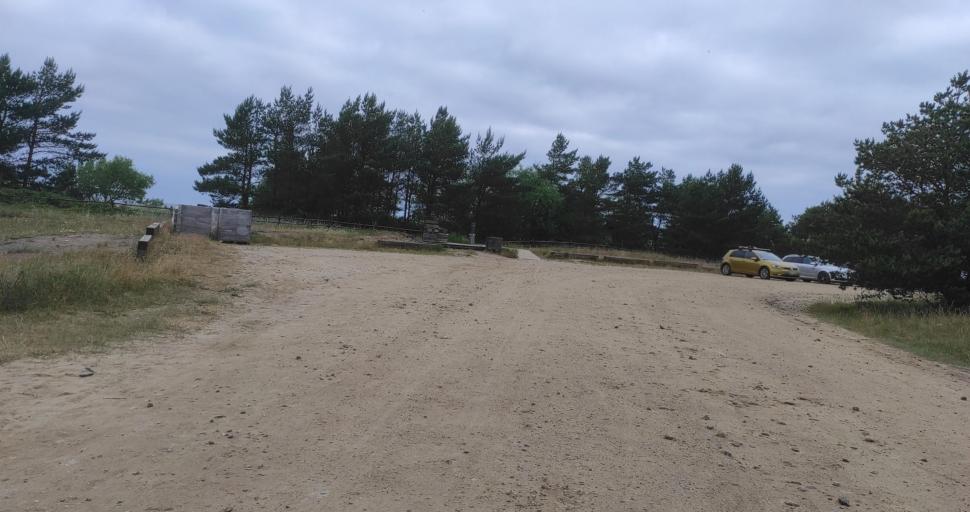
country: LV
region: Pavilostas
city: Pavilosta
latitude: 56.8927
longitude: 21.1853
